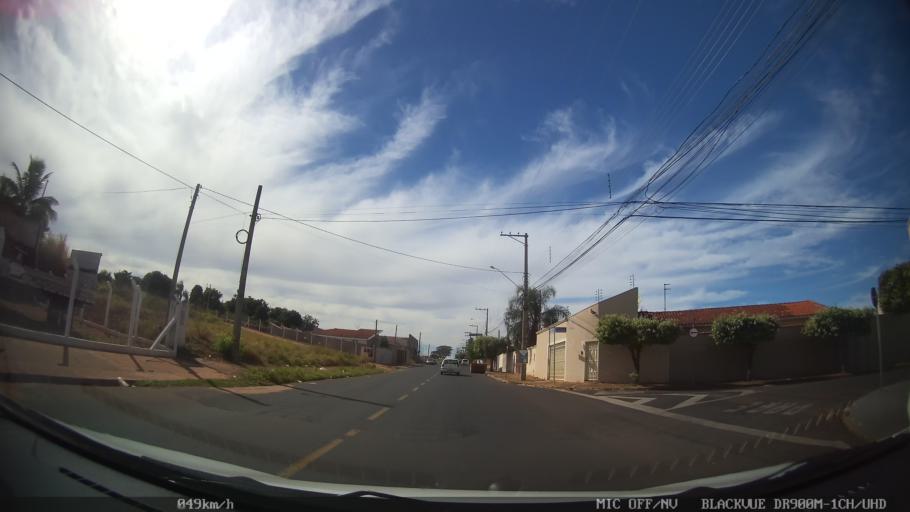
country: BR
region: Sao Paulo
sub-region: Catanduva
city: Catanduva
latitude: -21.1215
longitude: -48.9420
